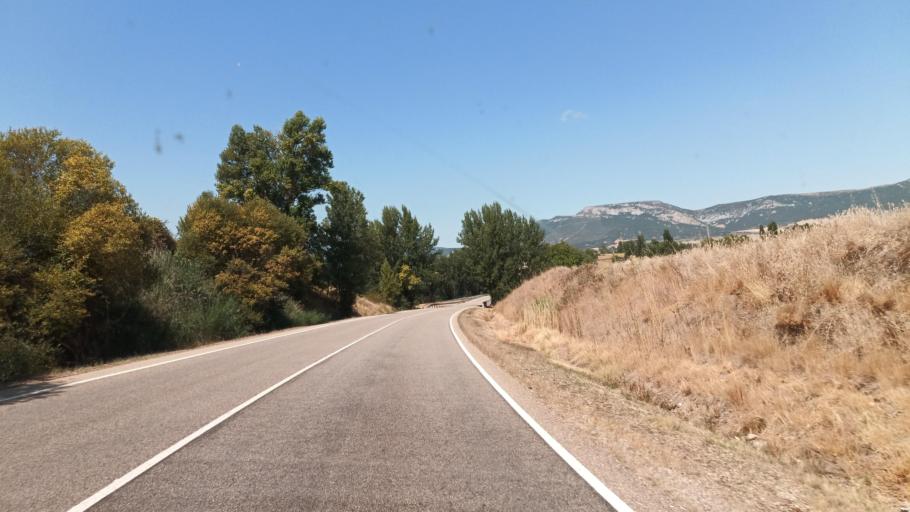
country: ES
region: Castille and Leon
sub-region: Provincia de Burgos
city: Quintanabureba
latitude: 42.6385
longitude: -3.3859
